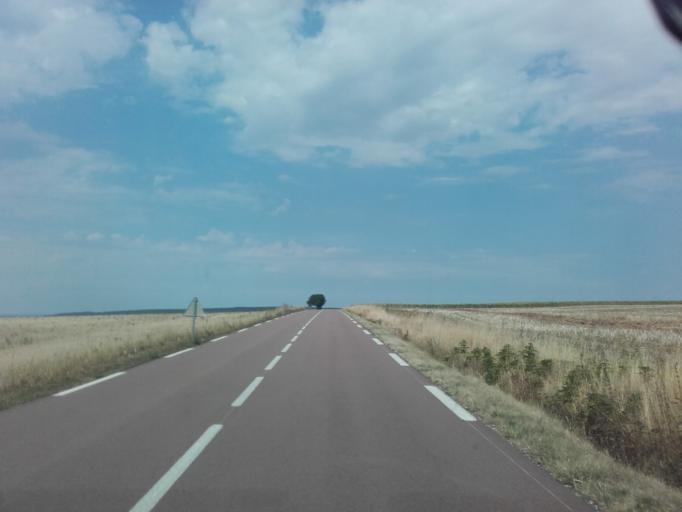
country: FR
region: Bourgogne
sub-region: Departement de l'Yonne
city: Joux-la-Ville
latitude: 47.7140
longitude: 3.8527
